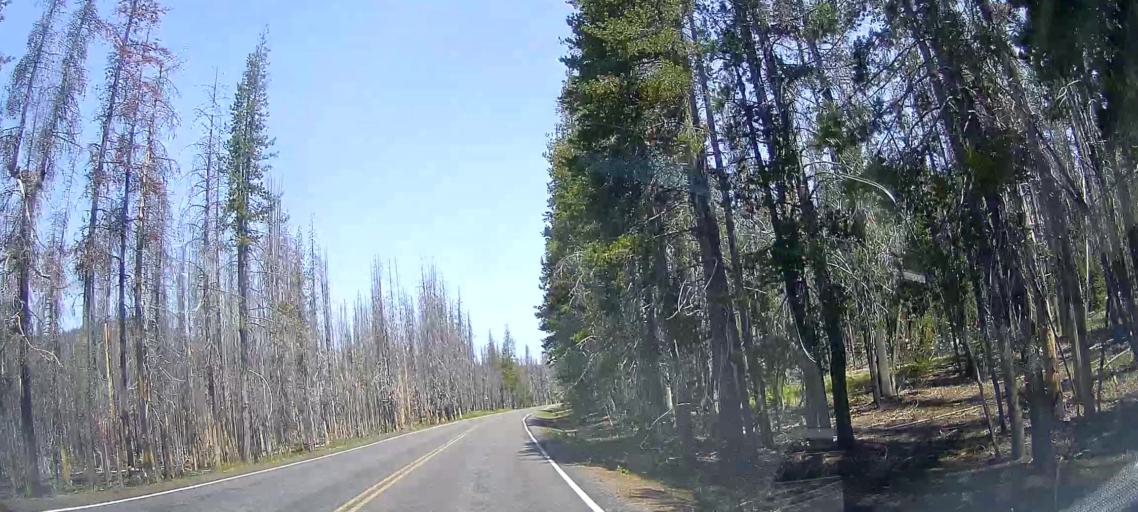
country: US
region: Oregon
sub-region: Lane County
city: Oakridge
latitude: 43.0519
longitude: -122.1220
